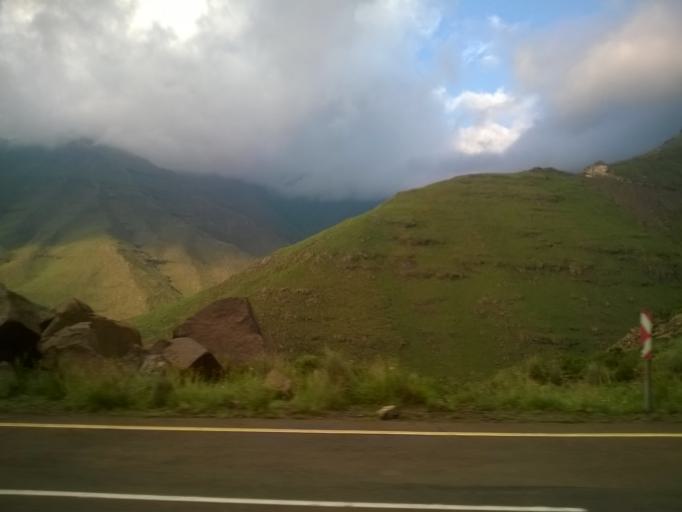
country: LS
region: Butha-Buthe
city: Butha-Buthe
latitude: -29.0693
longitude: 28.3720
